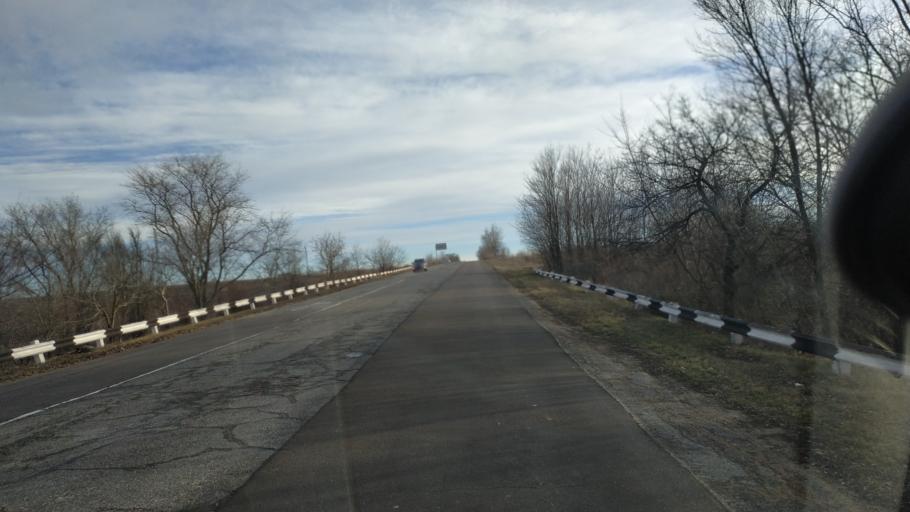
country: MD
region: Chisinau
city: Vadul lui Voda
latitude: 47.0737
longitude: 29.0219
